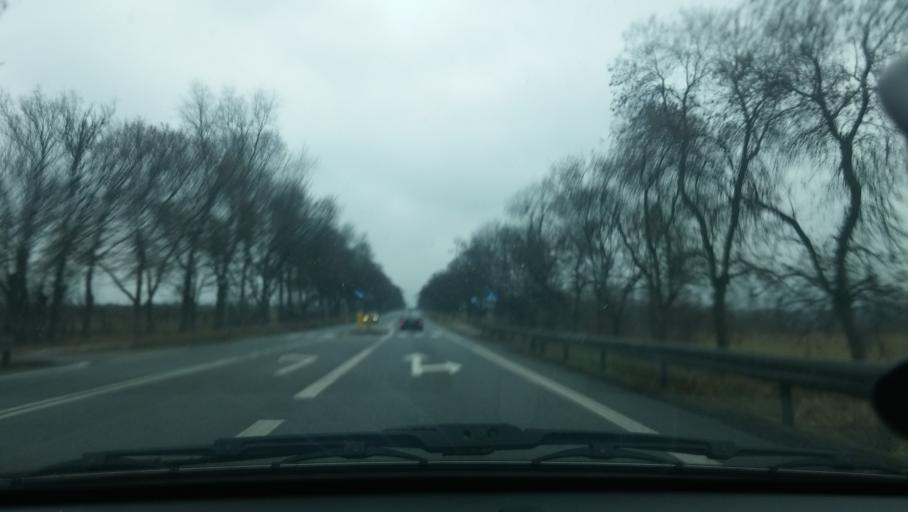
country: PL
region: Masovian Voivodeship
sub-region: Powiat wegrowski
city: Grebkow
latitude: 52.2069
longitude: 21.9221
